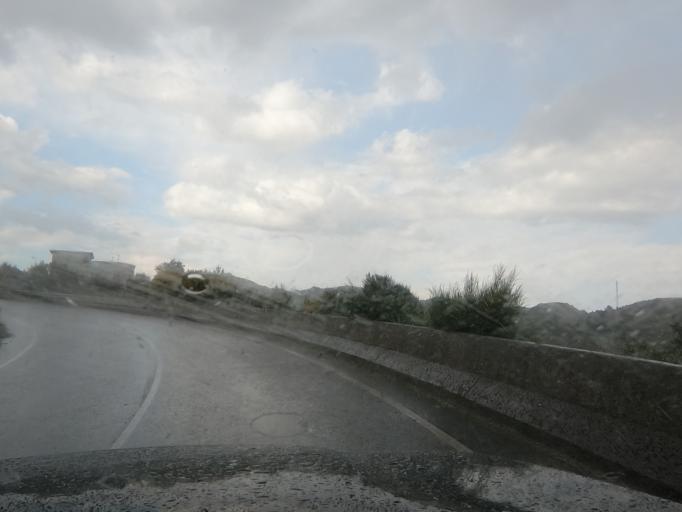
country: PT
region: Vila Real
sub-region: Vila Real
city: Vila Real
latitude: 41.3622
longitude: -7.6969
